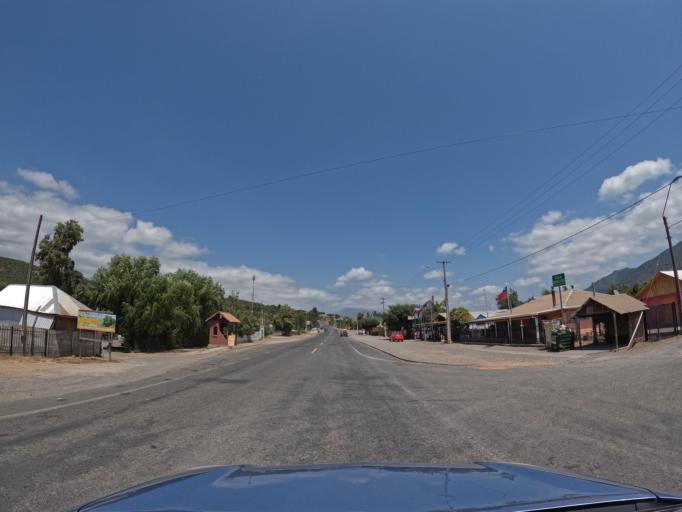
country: CL
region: Maule
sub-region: Provincia de Curico
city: Molina
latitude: -35.1776
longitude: -71.1210
